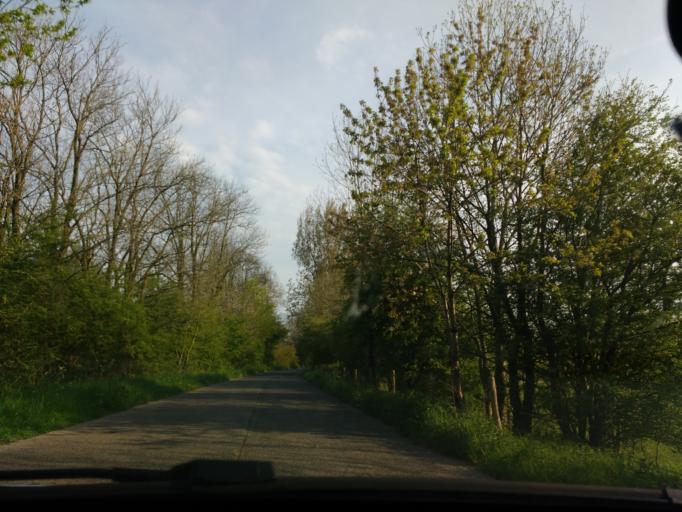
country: NL
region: Gelderland
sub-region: Gemeente Wageningen
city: Wageningen
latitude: 51.9468
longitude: 5.6203
